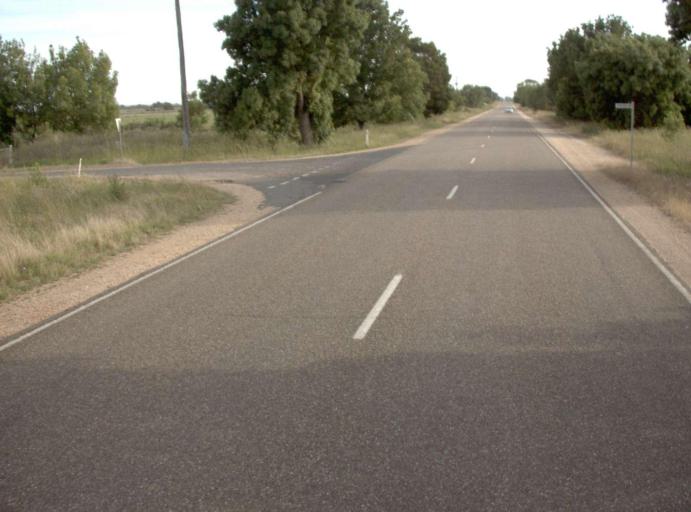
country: AU
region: Victoria
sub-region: Wellington
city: Heyfield
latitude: -37.9764
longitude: 146.8891
